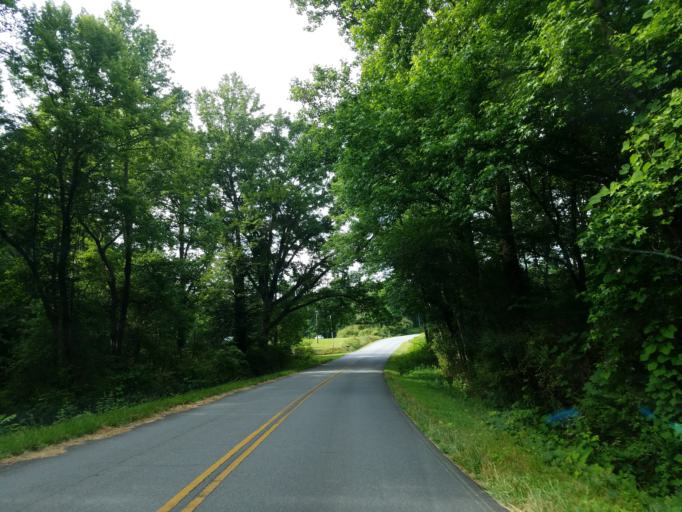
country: US
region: Georgia
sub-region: Dawson County
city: Dawsonville
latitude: 34.4724
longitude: -84.1790
